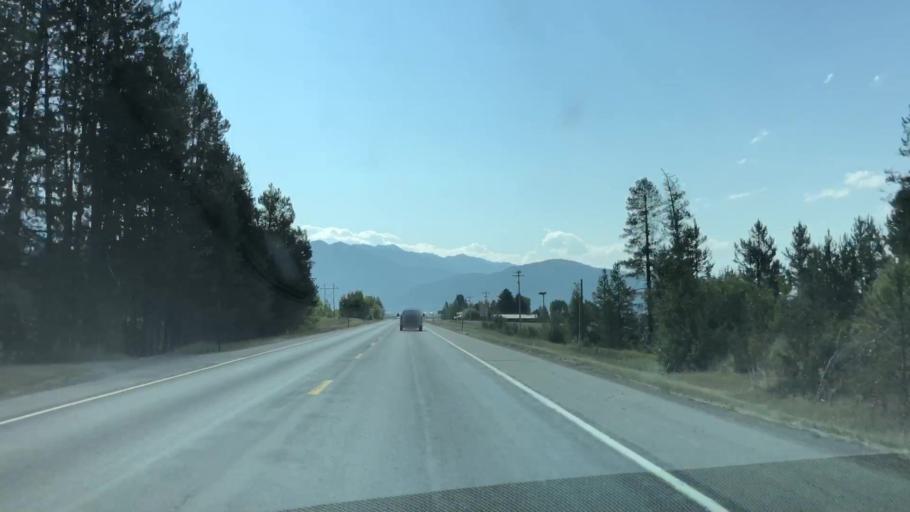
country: US
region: Wyoming
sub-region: Teton County
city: Hoback
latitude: 43.1961
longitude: -111.0400
